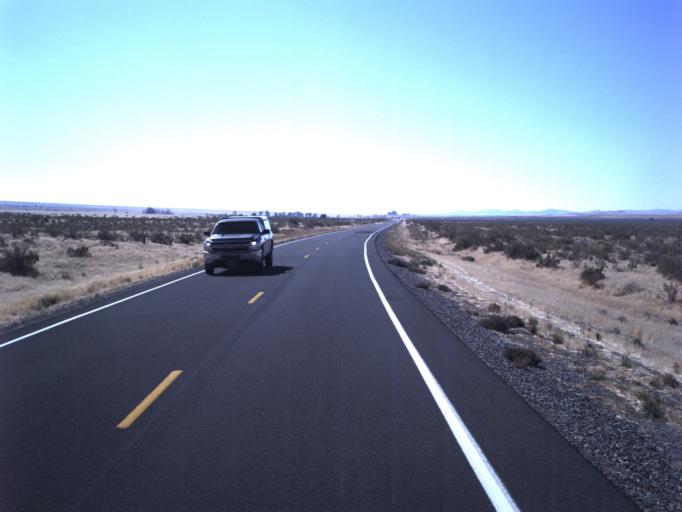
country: US
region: Utah
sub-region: Tooele County
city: Grantsville
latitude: 40.4823
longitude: -112.7454
